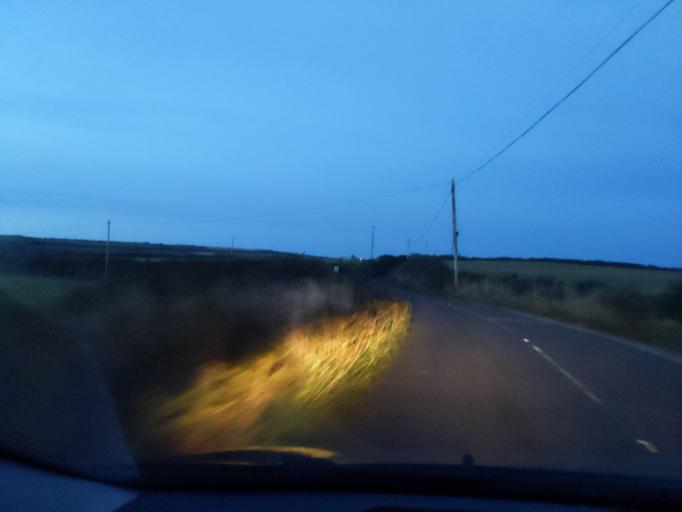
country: GB
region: England
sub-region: Cornwall
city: Camelford
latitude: 50.6956
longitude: -4.6691
